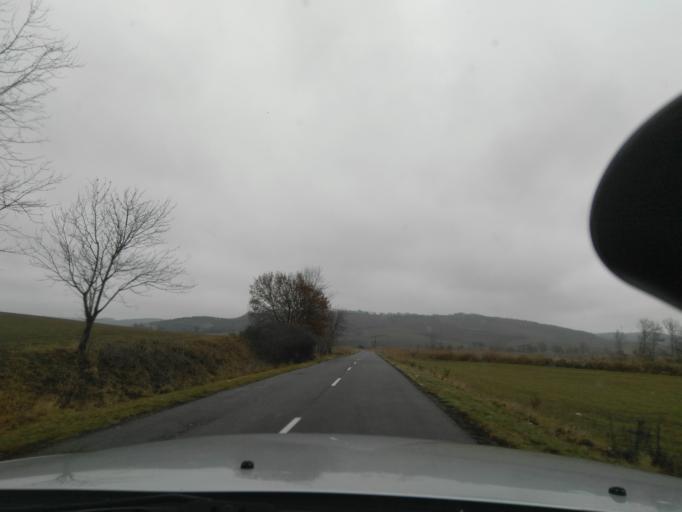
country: HU
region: Nograd
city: Kazar
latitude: 48.0356
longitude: 19.8729
